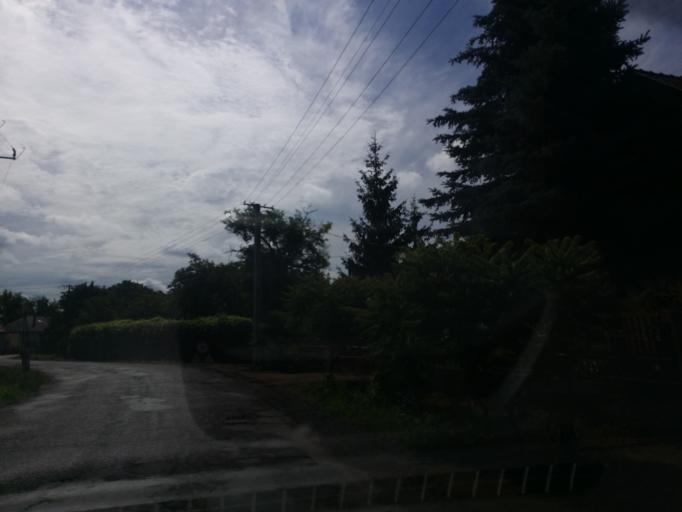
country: HU
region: Heves
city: Heves
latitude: 47.6170
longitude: 20.3570
